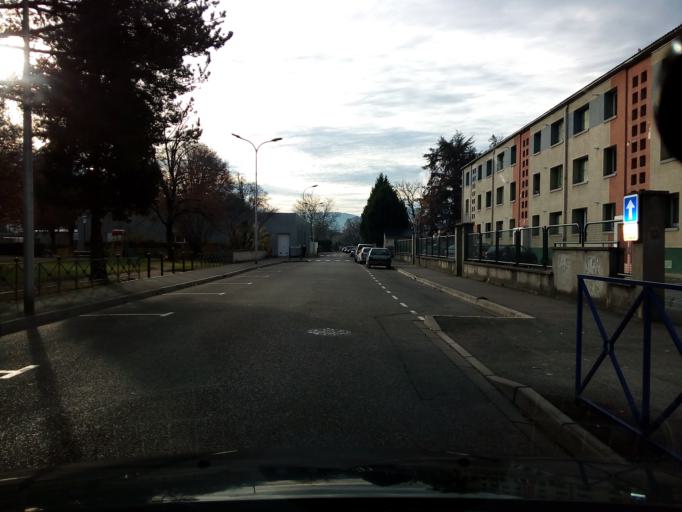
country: FR
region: Rhone-Alpes
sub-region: Departement de l'Isere
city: Saint-Martin-d'Heres
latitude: 45.1841
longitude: 5.7522
